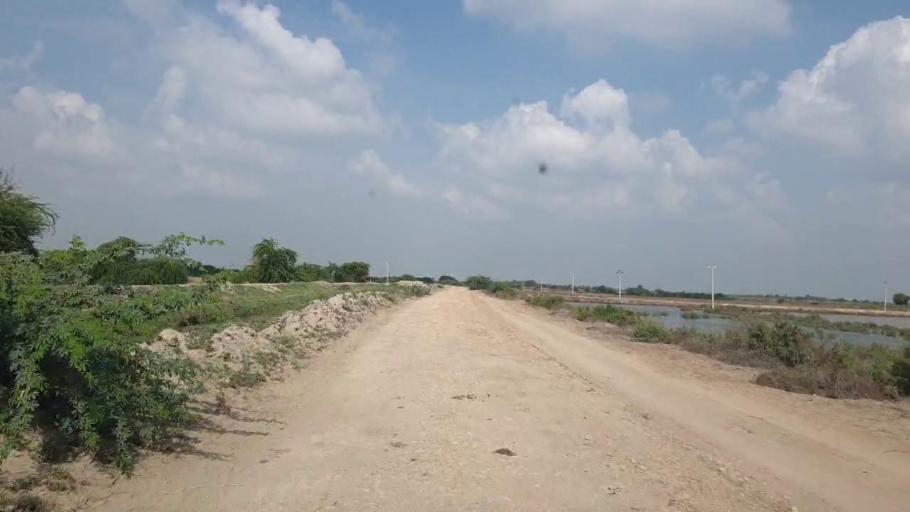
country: PK
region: Sindh
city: Badin
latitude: 24.5051
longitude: 68.6558
